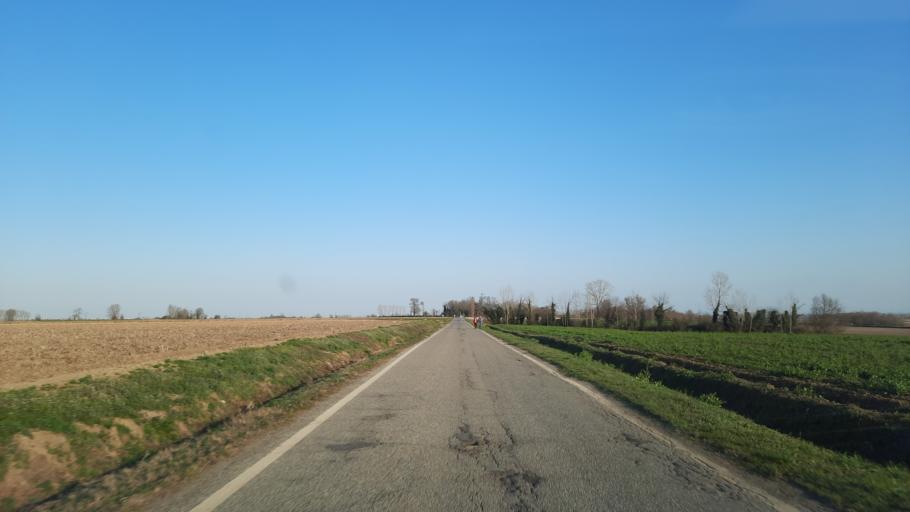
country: IT
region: Piedmont
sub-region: Provincia di Vercelli
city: Costanzana
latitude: 45.2053
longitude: 8.3512
